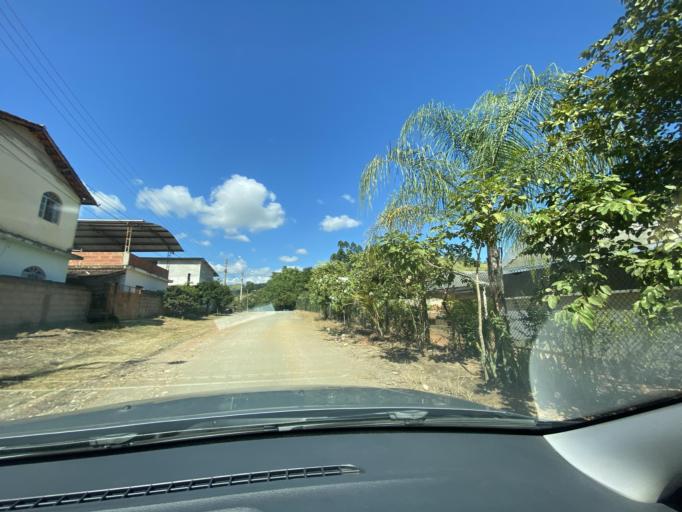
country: BR
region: Espirito Santo
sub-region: Jeronimo Monteiro
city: Jeronimo Monteiro
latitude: -20.7958
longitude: -41.4055
